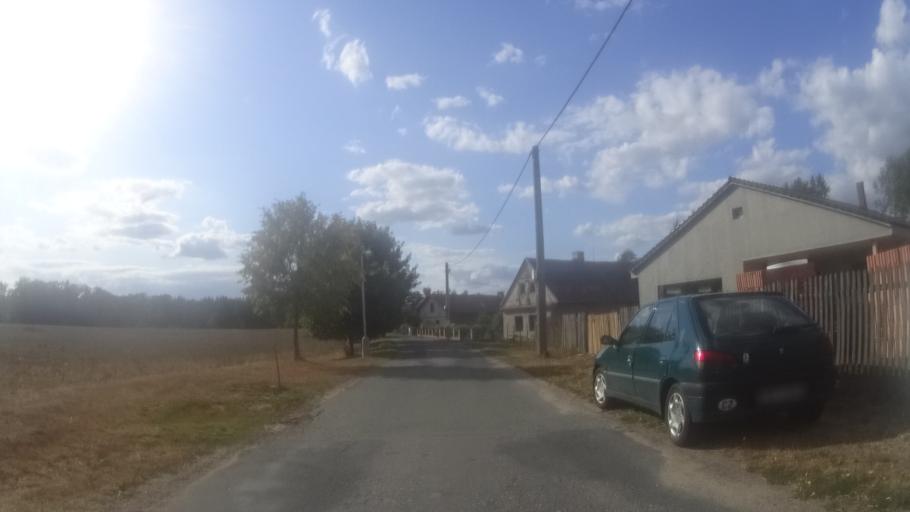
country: CZ
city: Albrechtice nad Orlici
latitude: 50.1562
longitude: 16.0449
